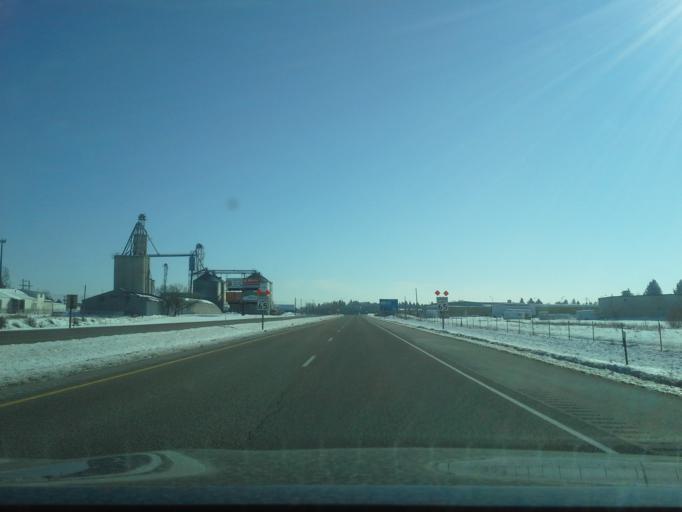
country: US
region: Idaho
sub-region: Bonneville County
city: Idaho Falls
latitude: 43.5134
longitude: -112.0578
